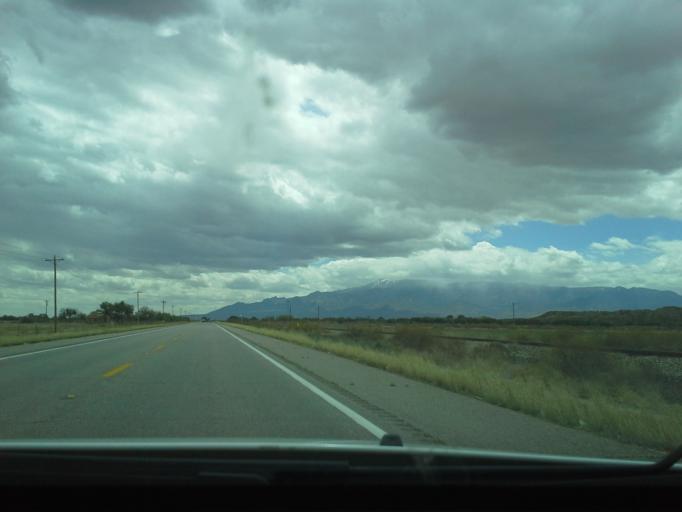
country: US
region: Arizona
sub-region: Graham County
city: Pima
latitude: 33.0006
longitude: -109.9433
